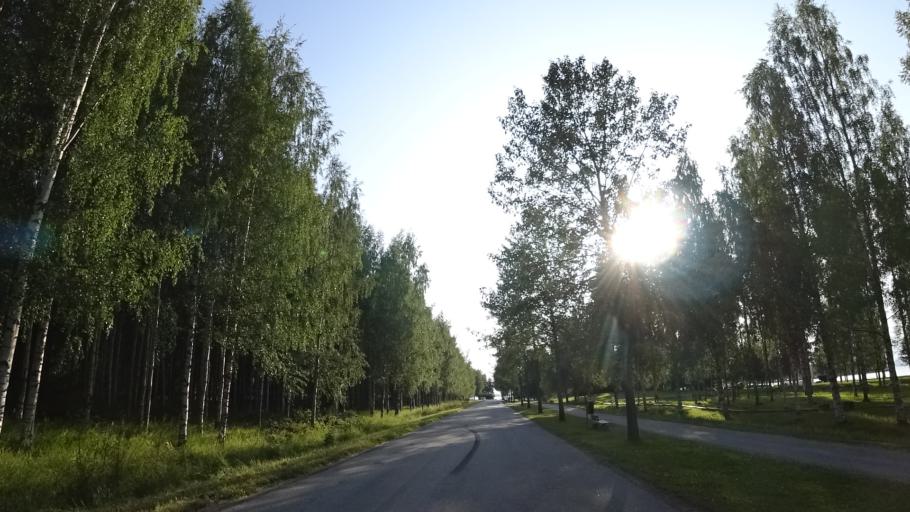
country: FI
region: North Karelia
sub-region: Pielisen Karjala
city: Lieksa
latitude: 63.3100
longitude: 30.0183
